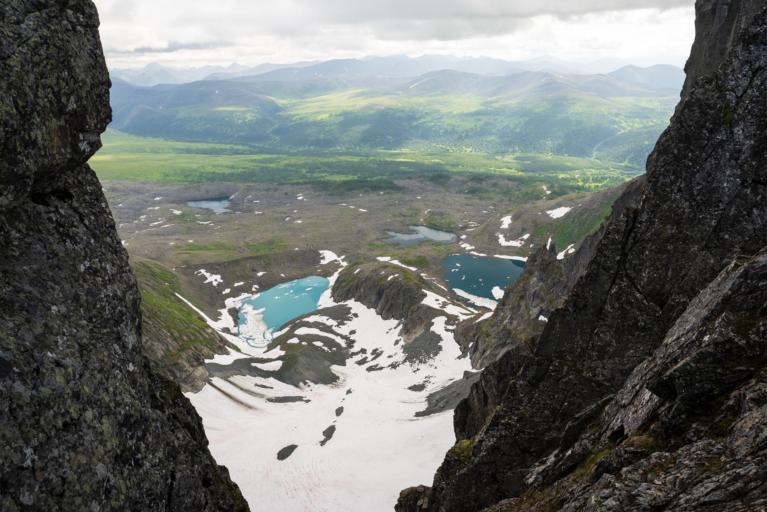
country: RU
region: Komi Republic
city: Synya
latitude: 64.7794
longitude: 58.8809
